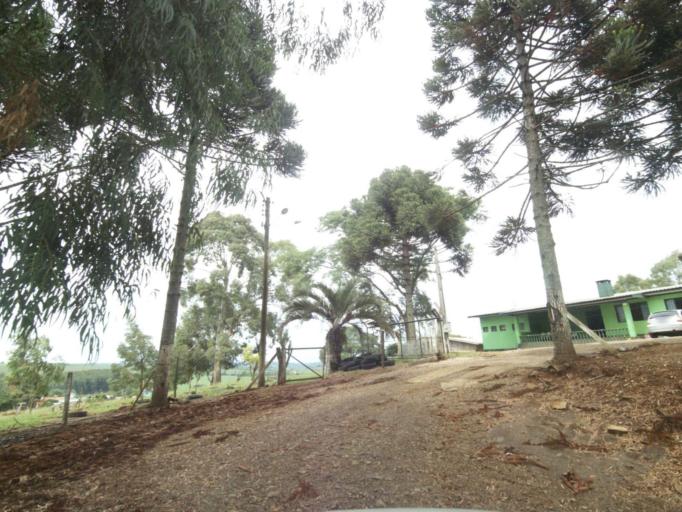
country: BR
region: Rio Grande do Sul
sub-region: Lagoa Vermelha
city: Lagoa Vermelha
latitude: -28.2268
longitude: -51.5166
